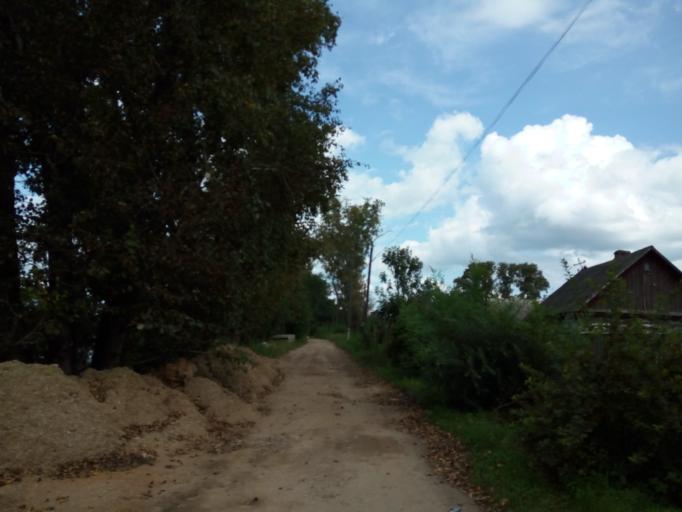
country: RU
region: Primorskiy
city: Dal'nerechensk
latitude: 45.9549
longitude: 133.8144
